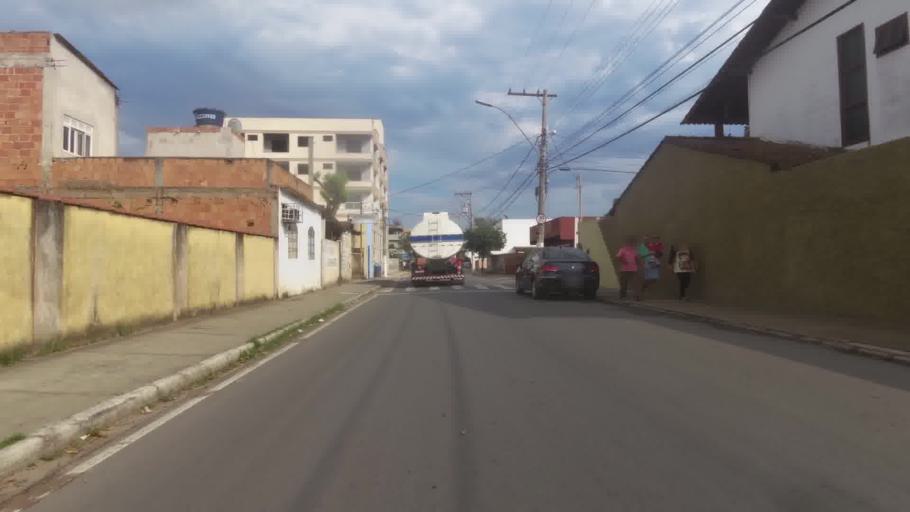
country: BR
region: Espirito Santo
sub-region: Piuma
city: Piuma
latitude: -20.8087
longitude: -40.6411
